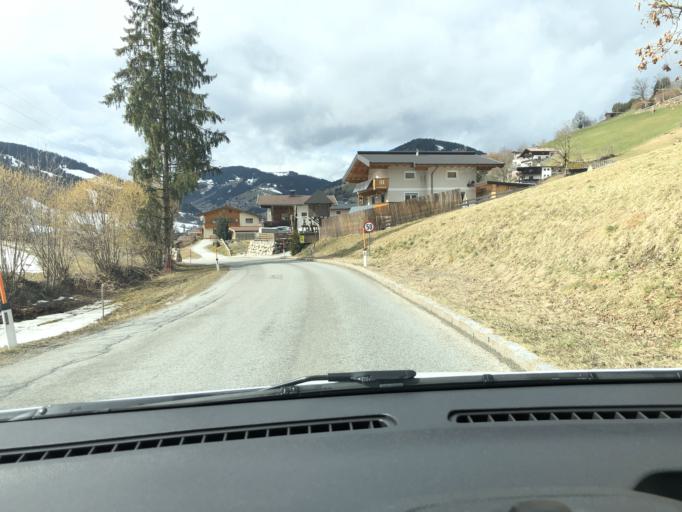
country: AT
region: Tyrol
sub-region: Politischer Bezirk Kitzbuhel
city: Itter
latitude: 47.4505
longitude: 12.1098
